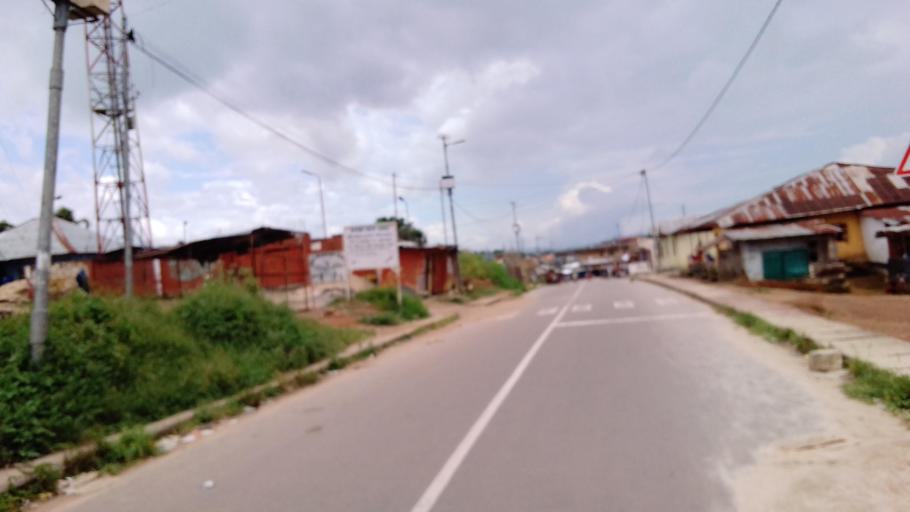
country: SL
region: Eastern Province
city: Koidu
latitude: 8.6457
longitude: -10.9755
